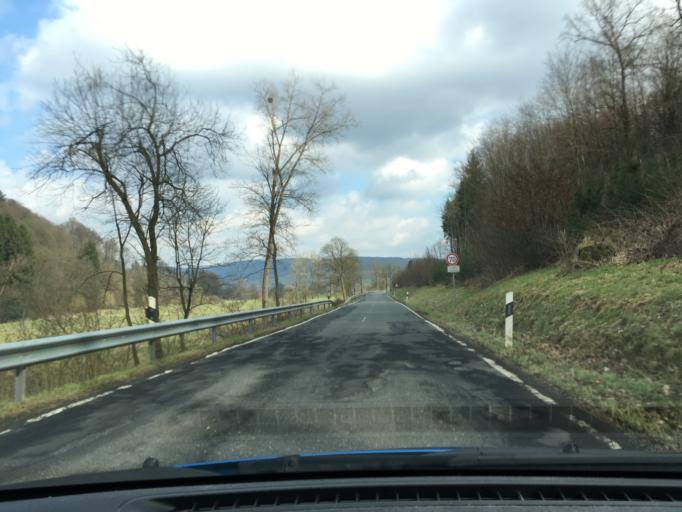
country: DE
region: Lower Saxony
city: Uslar
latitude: 51.6226
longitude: 9.6375
